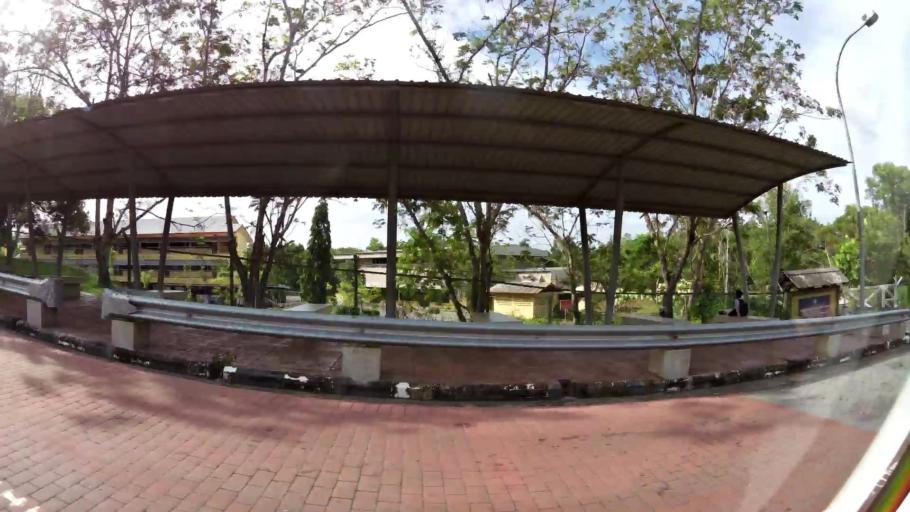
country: BN
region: Brunei and Muara
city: Bandar Seri Begawan
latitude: 4.9014
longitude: 114.8858
